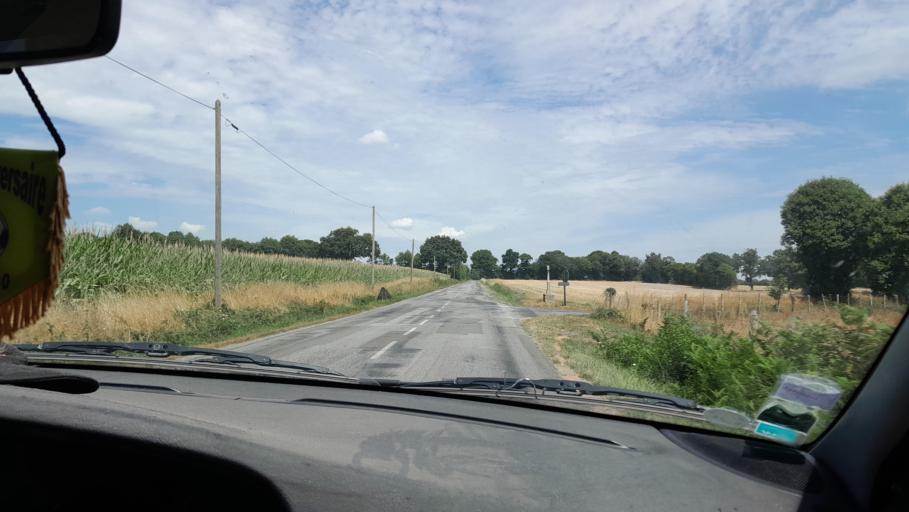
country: FR
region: Brittany
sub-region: Departement d'Ille-et-Vilaine
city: Le Pertre
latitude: 48.0526
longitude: -1.0338
